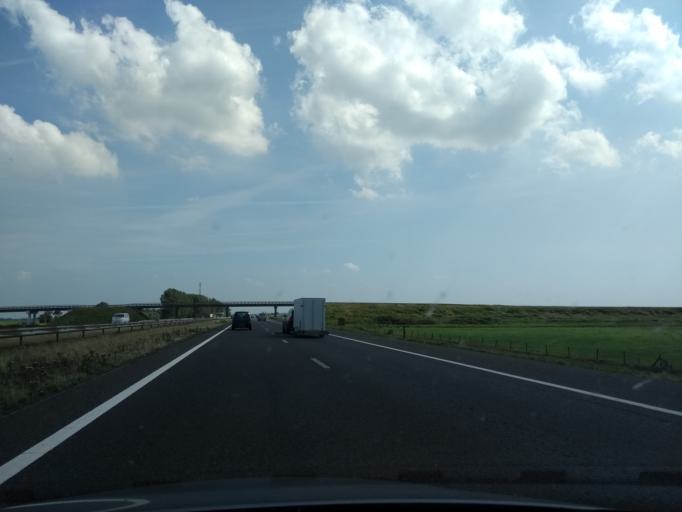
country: NL
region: Friesland
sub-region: Gemeente Skarsterlan
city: Joure
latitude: 52.9746
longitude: 5.7545
